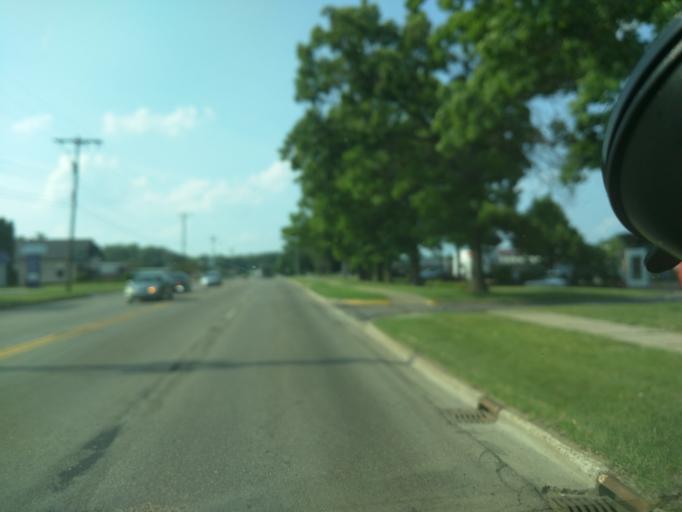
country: US
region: Michigan
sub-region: Jackson County
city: Jackson
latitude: 42.2727
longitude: -84.4529
